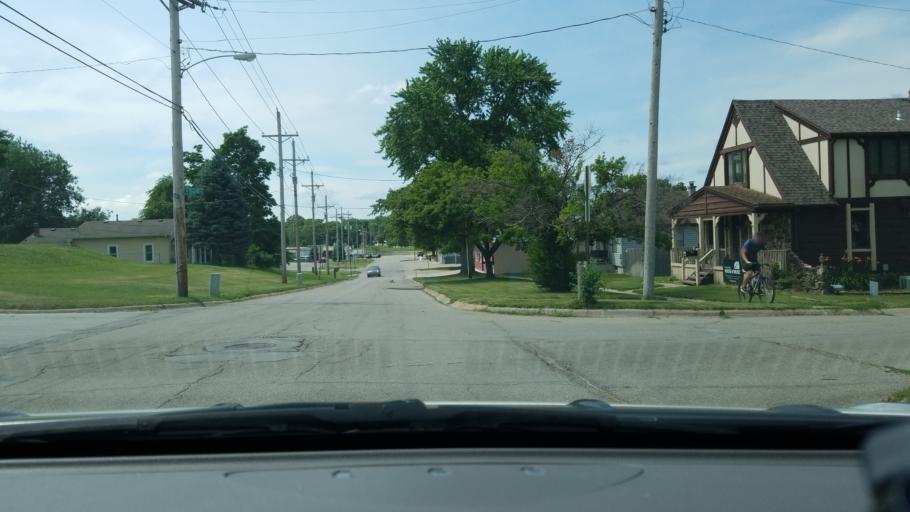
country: US
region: Nebraska
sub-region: Sarpy County
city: Papillion
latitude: 41.1595
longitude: -96.0443
